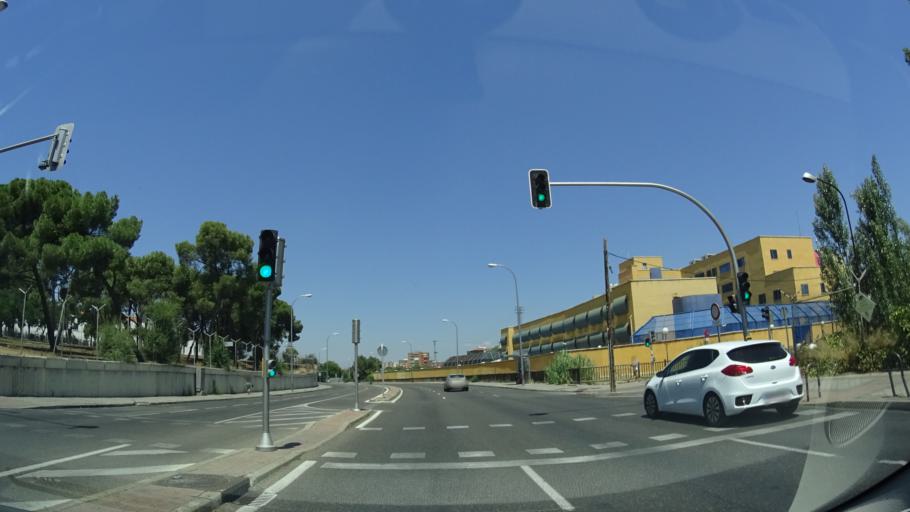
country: ES
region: Madrid
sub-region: Provincia de Madrid
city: Latina
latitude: 40.3819
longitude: -3.7577
